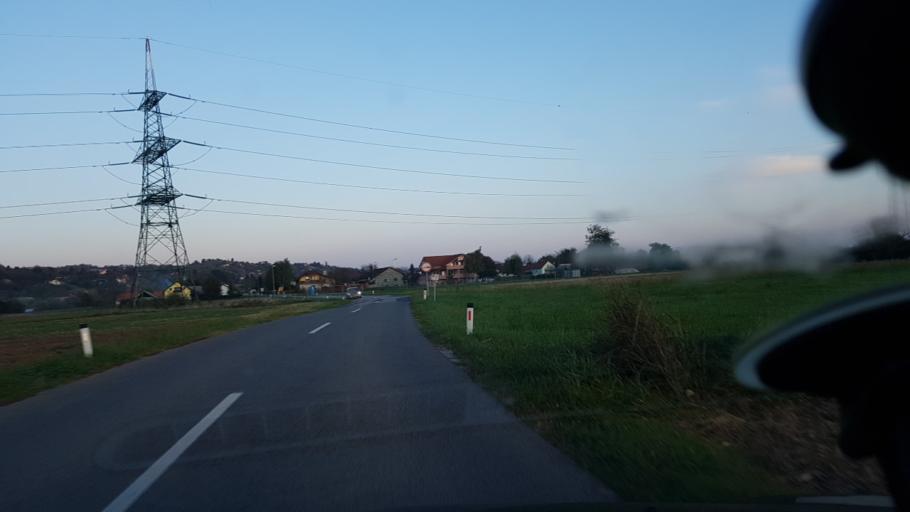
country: HR
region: Zagrebacka
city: Bregana
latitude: 45.8938
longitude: 15.6740
